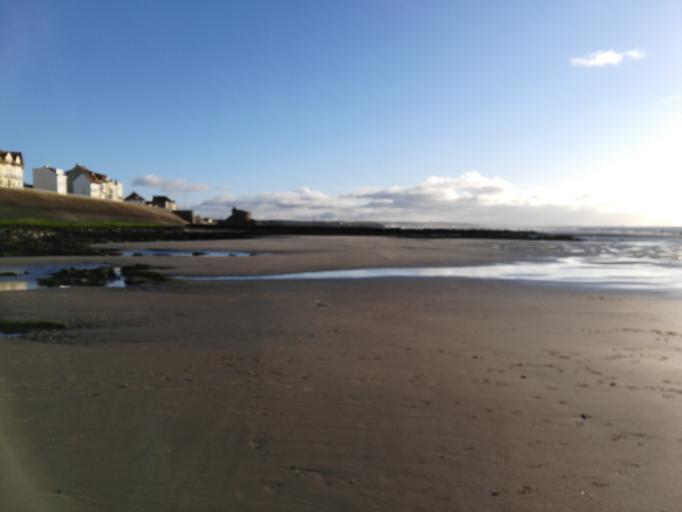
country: FR
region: Nord-Pas-de-Calais
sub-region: Departement du Pas-de-Calais
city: Ambleteuse
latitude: 50.8098
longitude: 1.5975
